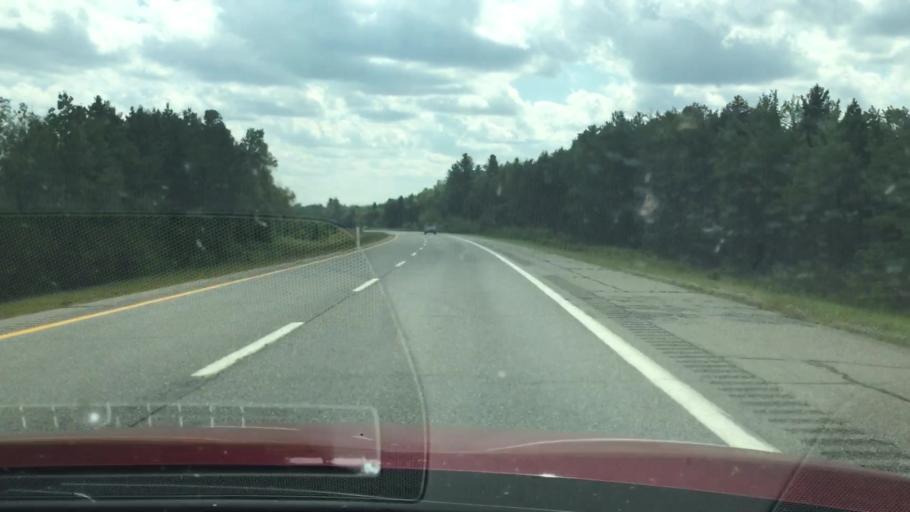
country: US
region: Maine
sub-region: Penobscot County
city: Howland
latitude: 45.2717
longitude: -68.6787
